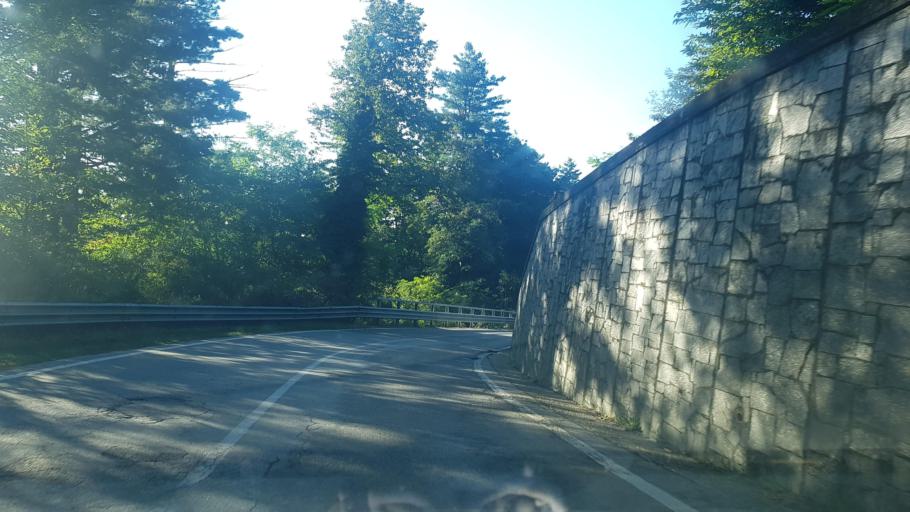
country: IT
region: Piedmont
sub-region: Provincia Verbano-Cusio-Ossola
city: Bee
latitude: 45.9699
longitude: 8.5827
